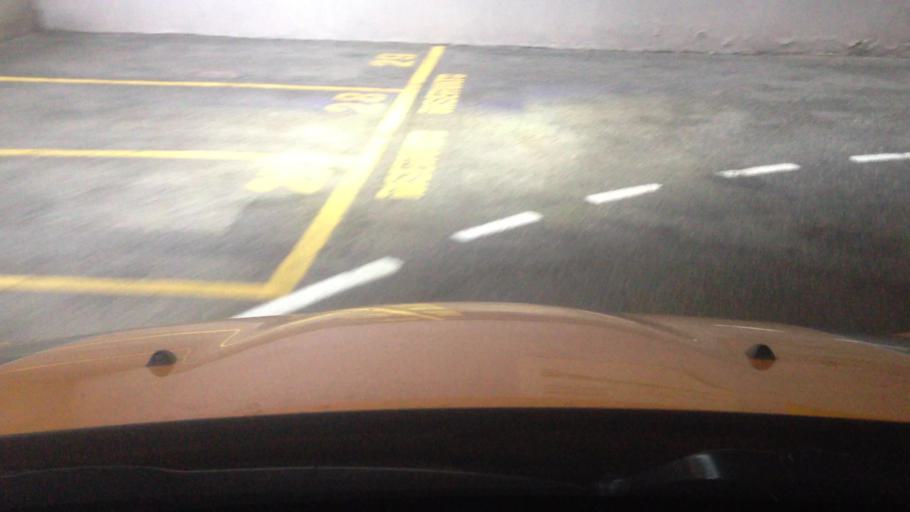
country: CH
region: Ticino
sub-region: Mendrisio District
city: Chiasso
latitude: 45.8348
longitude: 9.0311
